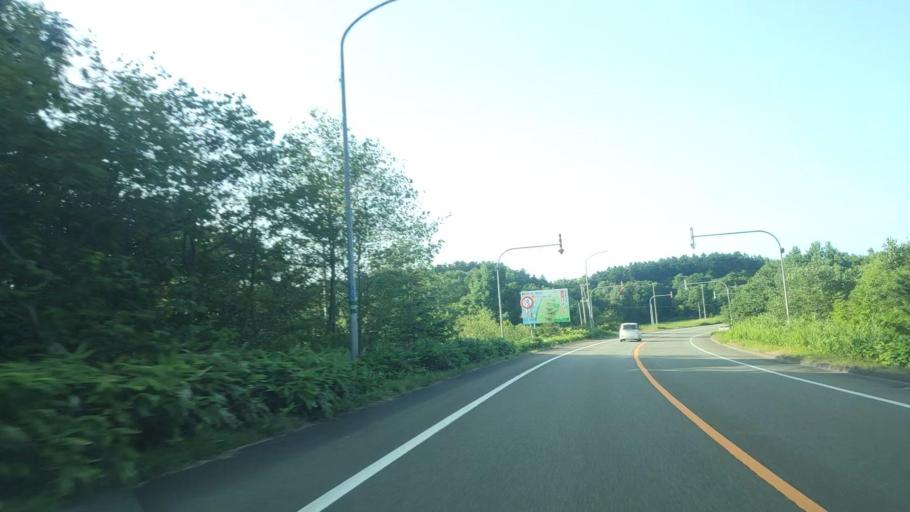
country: JP
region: Hokkaido
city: Makubetsu
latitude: 45.0787
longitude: 141.7533
